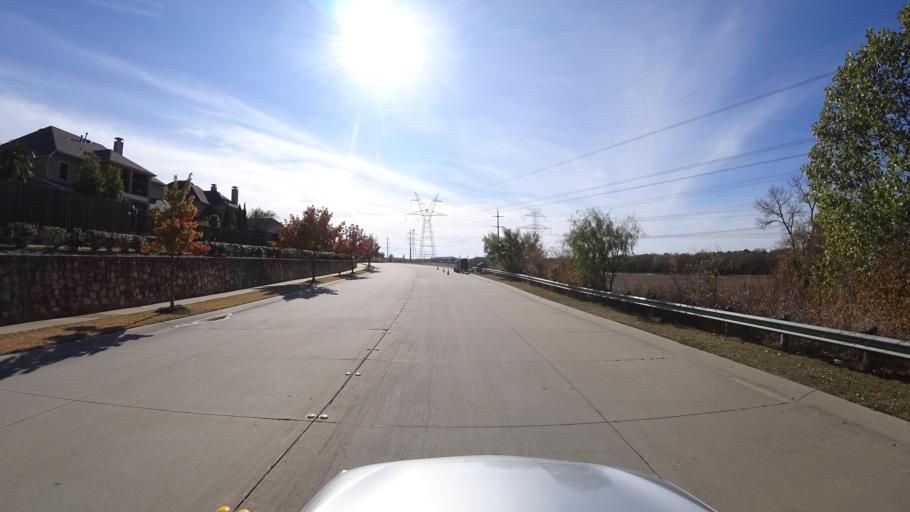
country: US
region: Texas
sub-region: Denton County
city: The Colony
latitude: 33.0297
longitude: -96.9131
